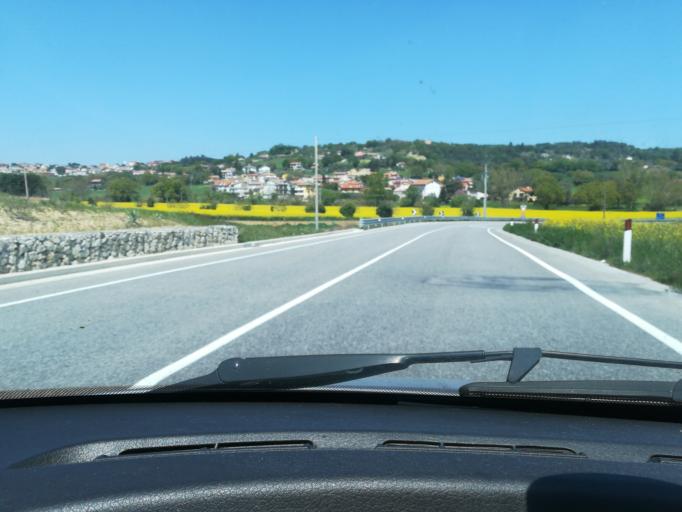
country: IT
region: The Marches
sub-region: Provincia di Ancona
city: Villa Musone
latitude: 43.4564
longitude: 13.5813
